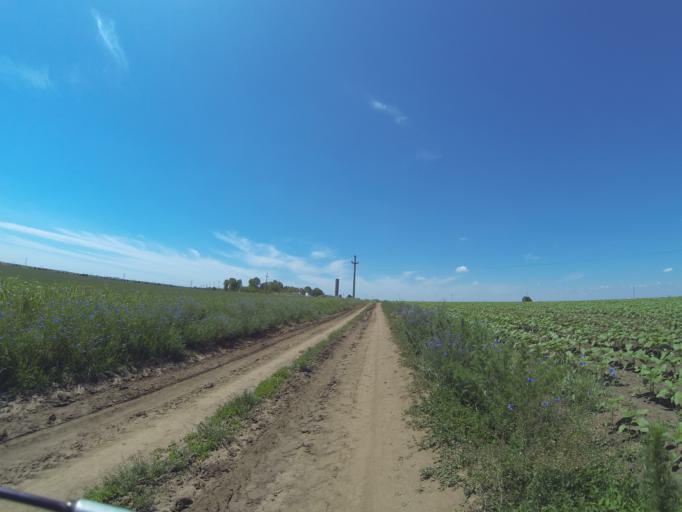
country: RO
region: Dolj
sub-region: Comuna Leu
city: Zanoaga
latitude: 44.1984
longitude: 24.0586
